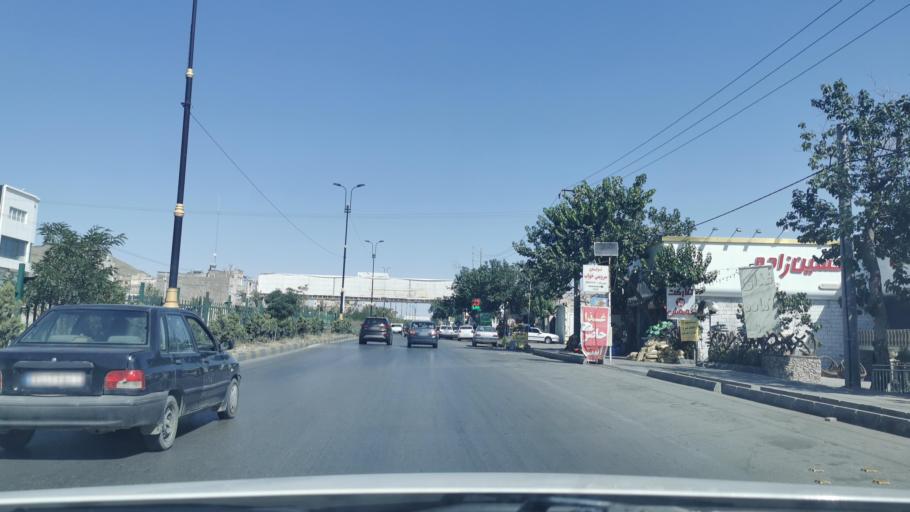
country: IR
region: Razavi Khorasan
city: Torqabeh
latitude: 36.3976
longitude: 59.3944
